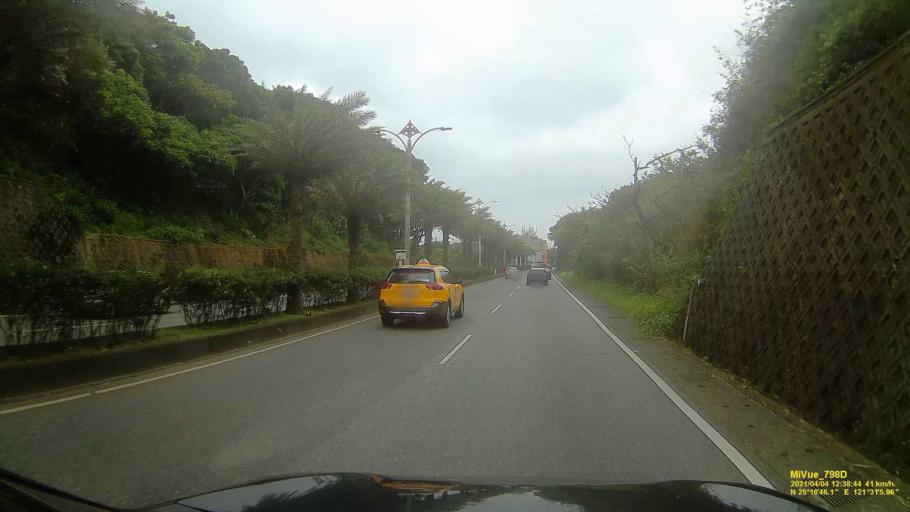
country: TW
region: Taipei
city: Taipei
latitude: 25.2792
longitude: 121.5183
